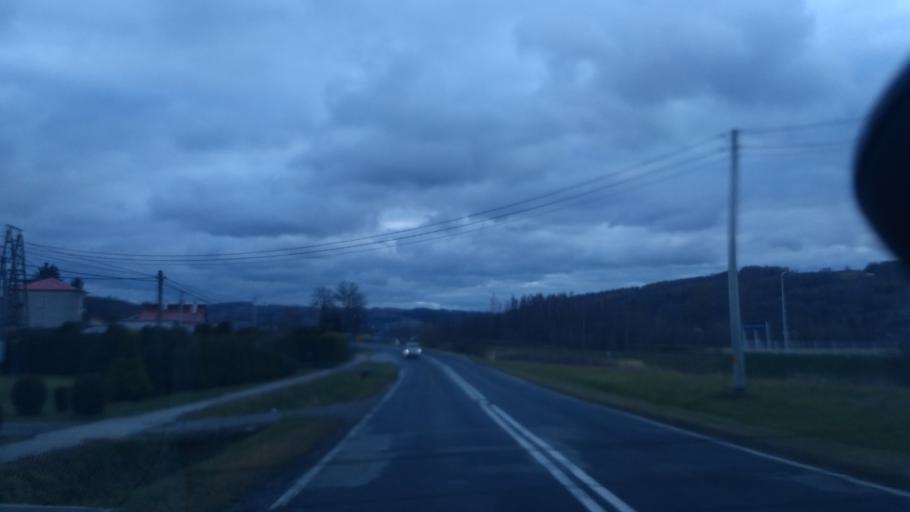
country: PL
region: Subcarpathian Voivodeship
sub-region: Powiat strzyzowski
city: Czudec
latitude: 49.9248
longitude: 21.8200
